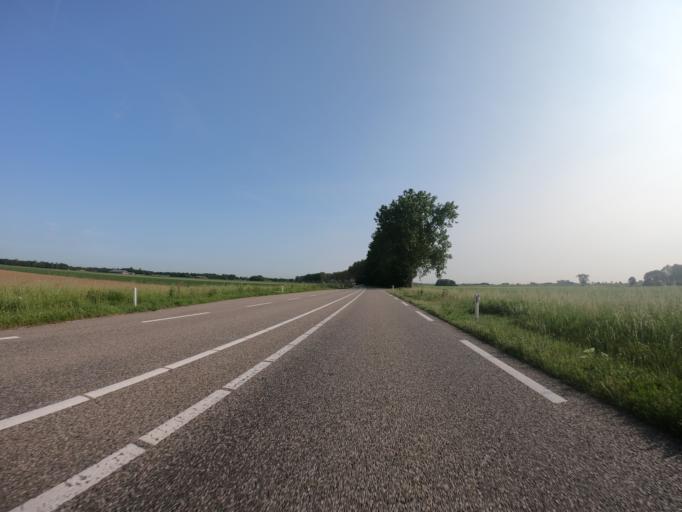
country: NL
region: North Brabant
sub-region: Gemeente Landerd
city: Reek
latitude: 51.7592
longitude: 5.6690
